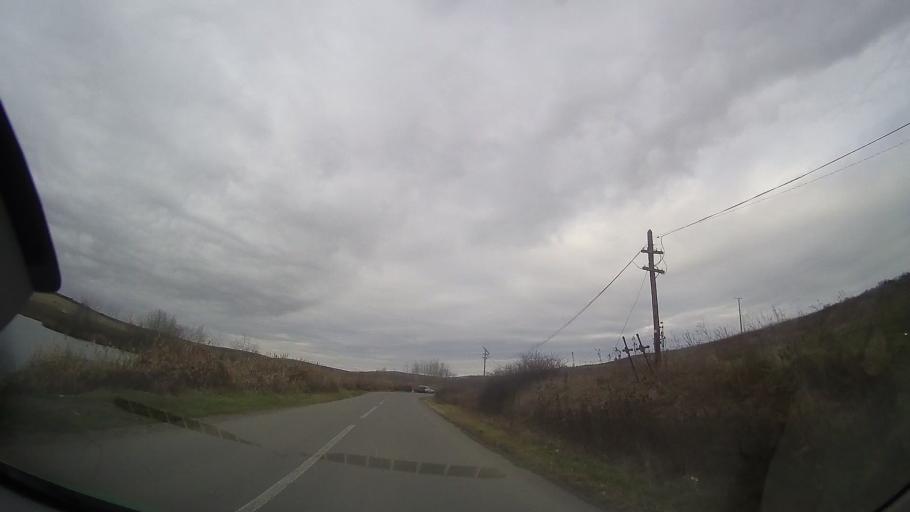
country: RO
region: Mures
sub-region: Comuna Faragau
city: Faragau
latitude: 46.7450
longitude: 24.5324
